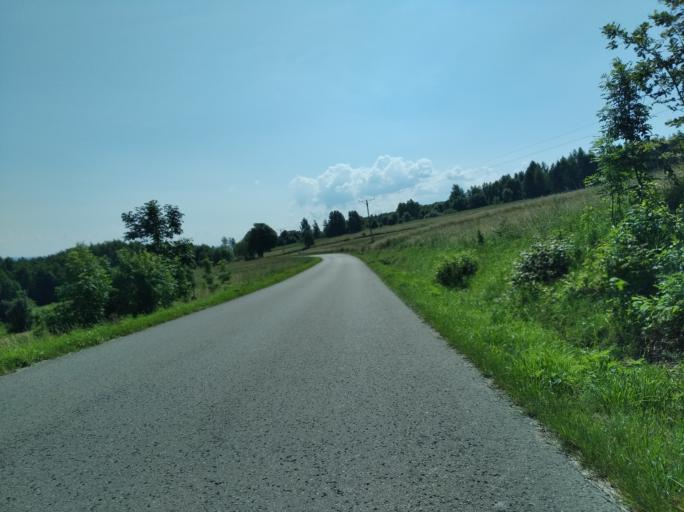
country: PL
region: Subcarpathian Voivodeship
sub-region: Powiat rzeszowski
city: Dynow
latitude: 49.8131
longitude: 22.2085
